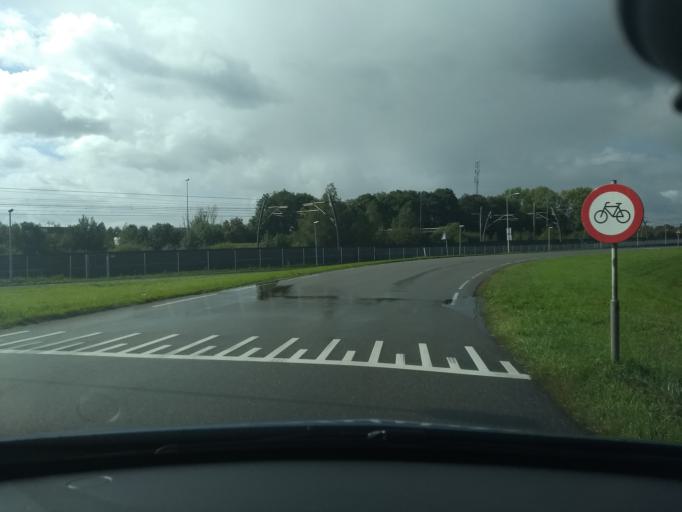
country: NL
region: South Holland
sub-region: Gemeente Gorinchem
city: Gorinchem
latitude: 51.8455
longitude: 4.9992
